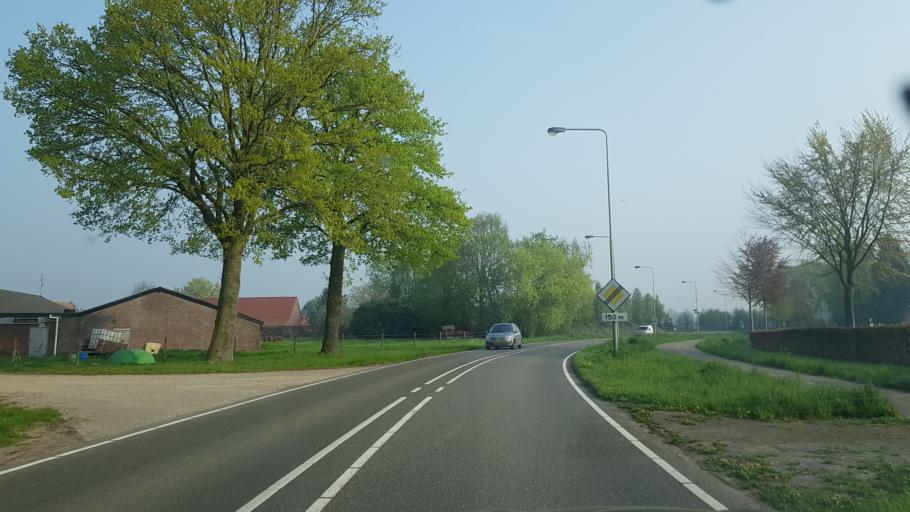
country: NL
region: Limburg
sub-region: Gemeente Nederweert
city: Nederweert
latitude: 51.2862
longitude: 5.7333
